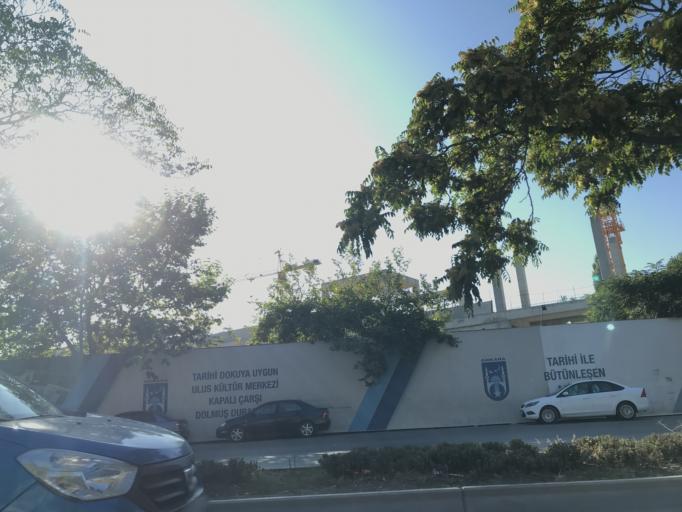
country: TR
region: Ankara
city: Ankara
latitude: 39.9460
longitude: 32.8608
